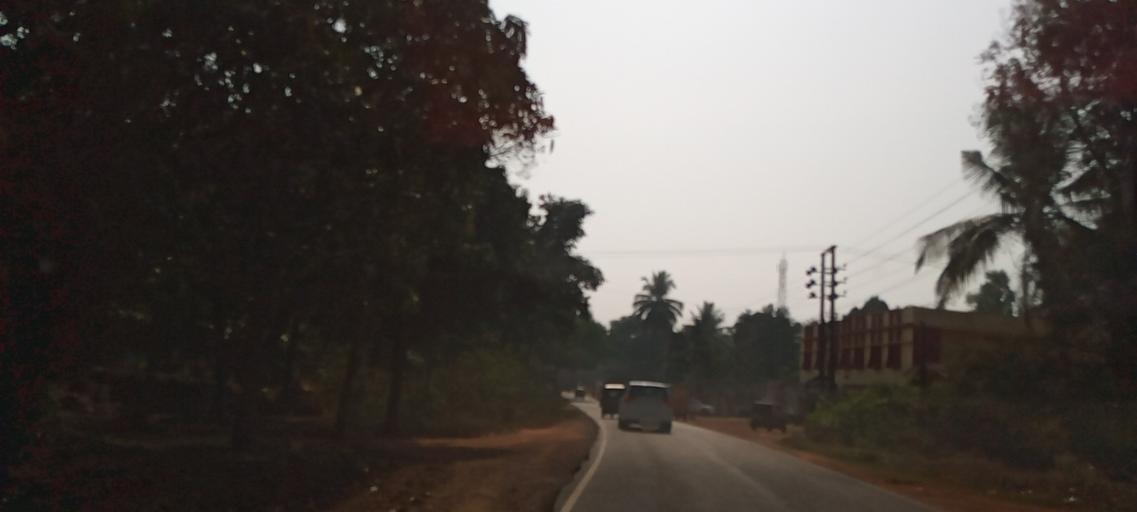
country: IN
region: Karnataka
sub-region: Udupi
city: Coondapoor
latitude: 13.5135
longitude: 74.7712
